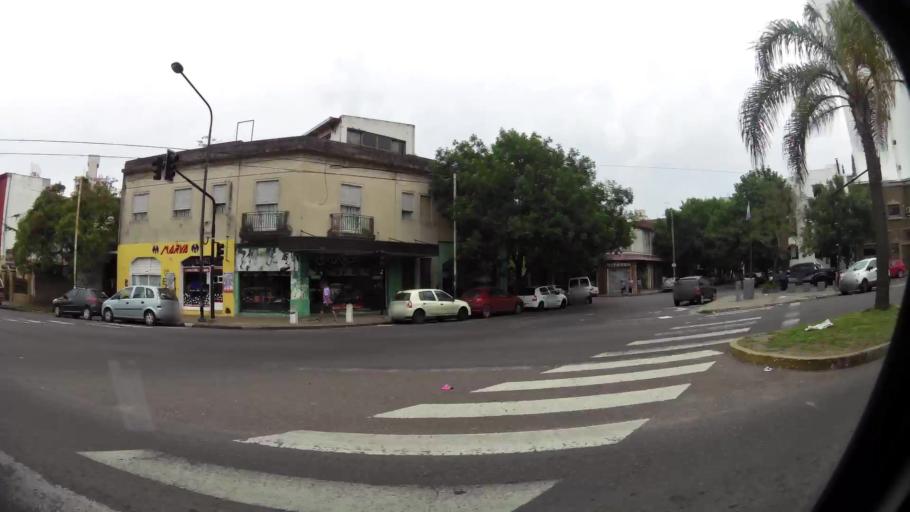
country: AR
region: Buenos Aires
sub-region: Partido de La Plata
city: La Plata
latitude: -34.9249
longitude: -57.9543
